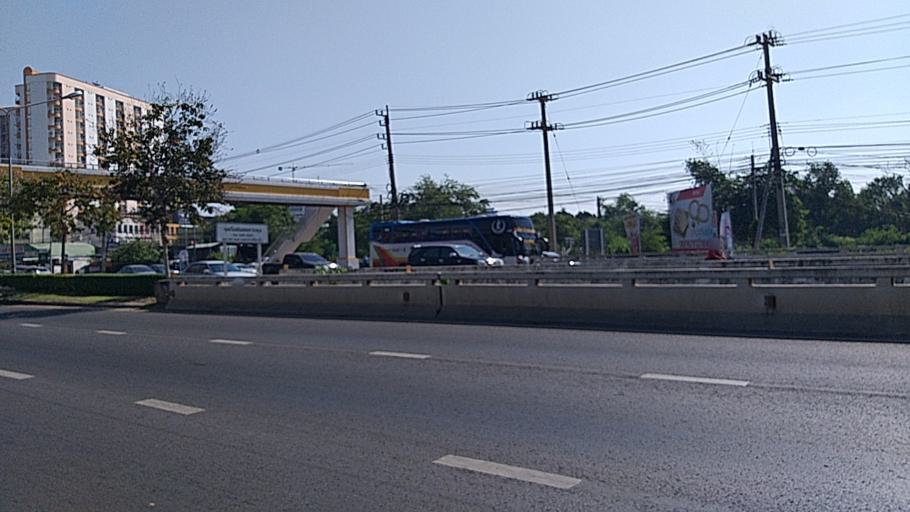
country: TH
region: Nakhon Ratchasima
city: Nakhon Ratchasima
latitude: 14.9844
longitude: 102.0930
